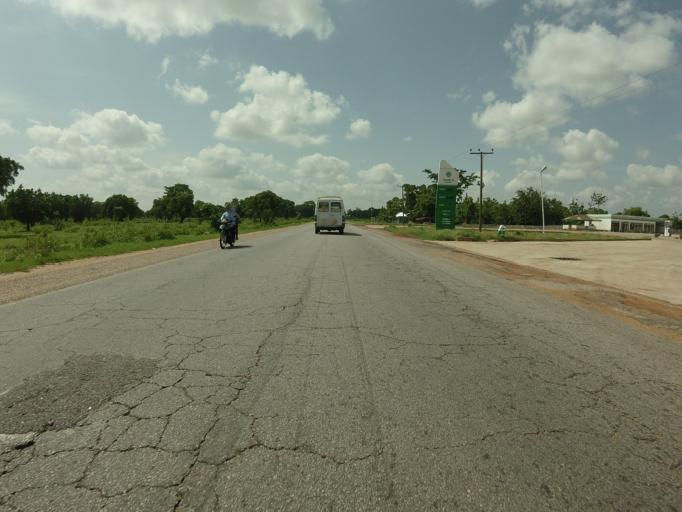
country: GH
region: Northern
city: Savelugu
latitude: 9.5712
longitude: -0.8350
